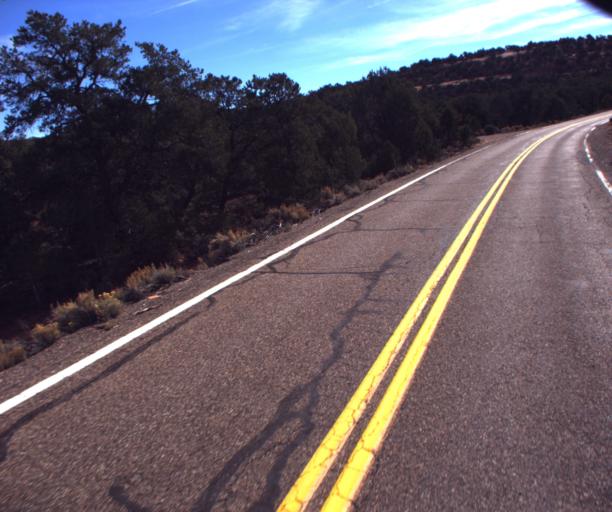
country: US
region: Arizona
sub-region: Navajo County
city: Kayenta
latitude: 36.6550
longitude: -110.5200
